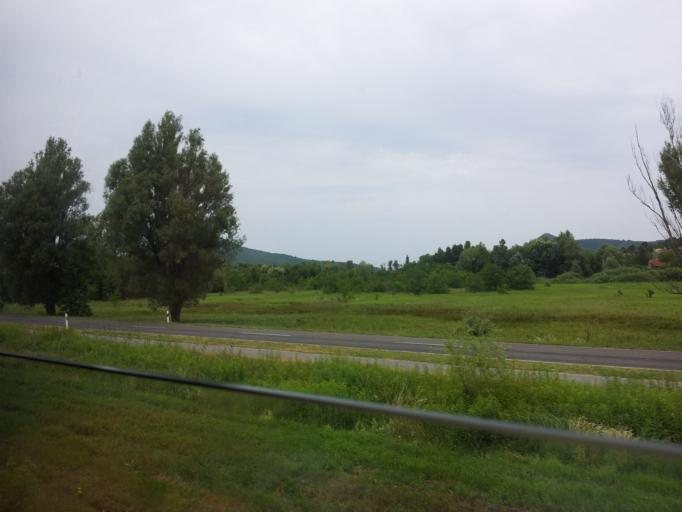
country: HU
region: Veszprem
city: Badacsonytomaj
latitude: 46.8076
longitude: 17.5257
